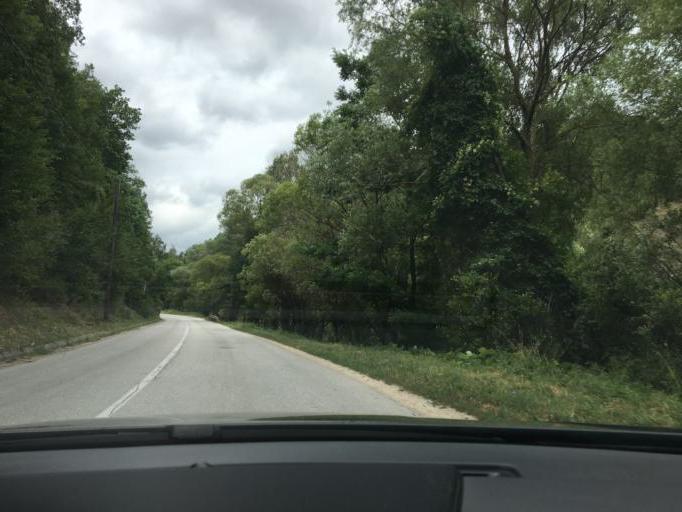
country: MK
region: Kriva Palanka
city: Kriva Palanka
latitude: 42.2273
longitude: 22.3597
